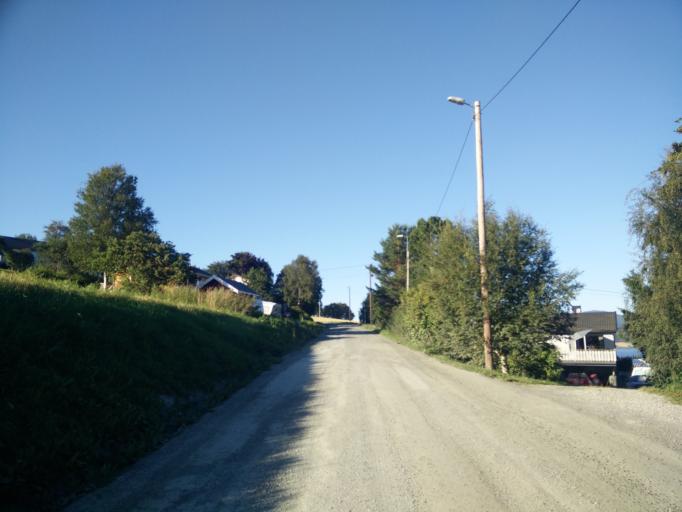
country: NO
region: Sor-Trondelag
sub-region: Skaun
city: Borsa
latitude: 63.3285
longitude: 10.0639
